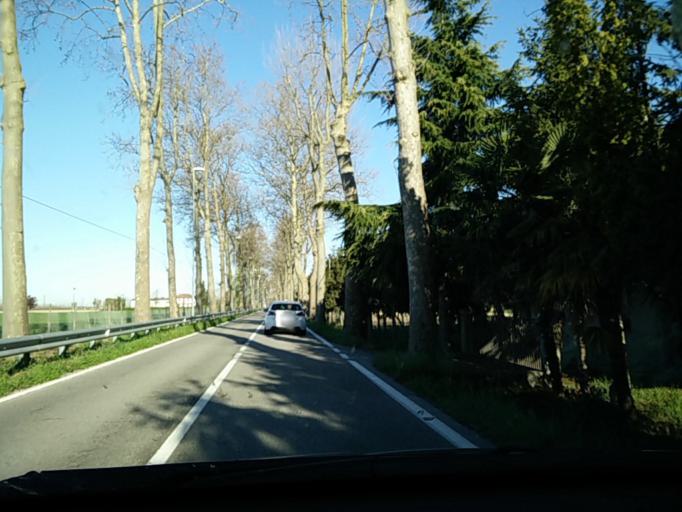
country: IT
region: Veneto
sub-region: Provincia di Venezia
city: Quarto d'Altino
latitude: 45.5653
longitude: 12.4020
